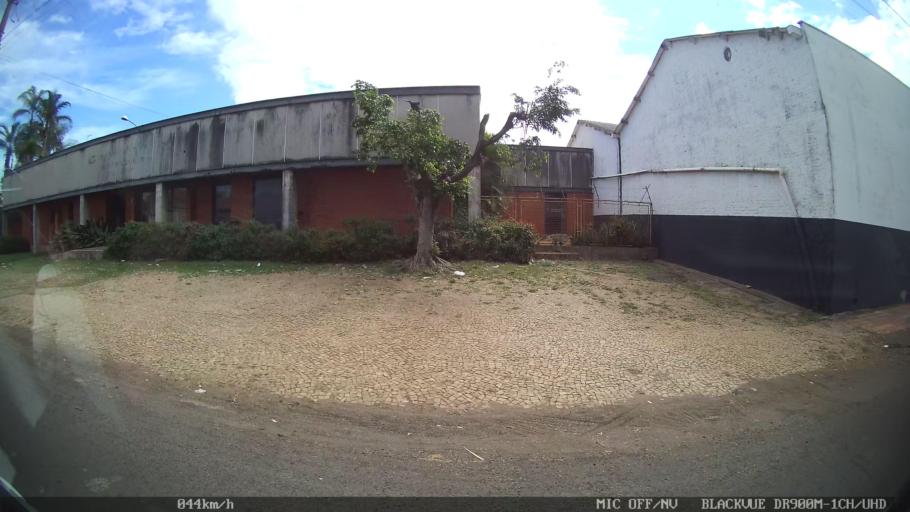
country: BR
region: Sao Paulo
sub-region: Bady Bassitt
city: Bady Bassitt
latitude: -20.8149
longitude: -49.5170
